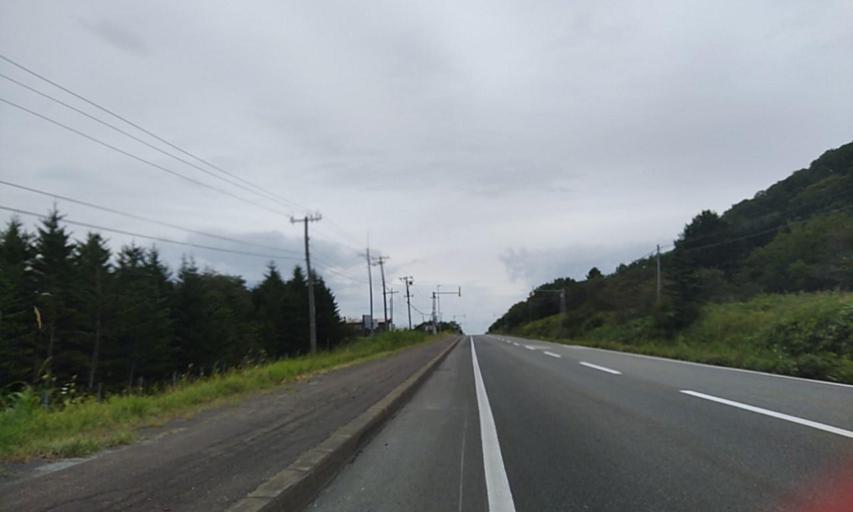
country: JP
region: Hokkaido
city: Nayoro
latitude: 45.0263
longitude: 142.5288
